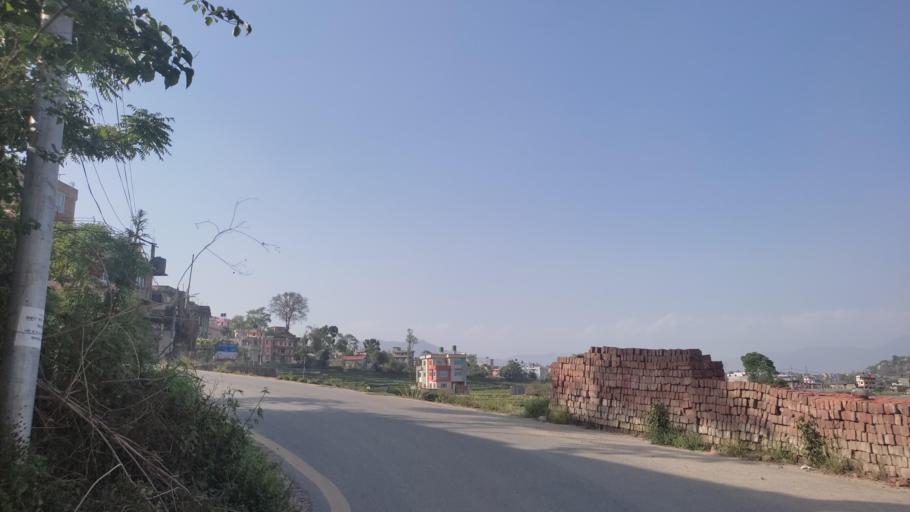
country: NP
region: Central Region
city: Kirtipur
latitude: 27.6507
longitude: 85.2774
